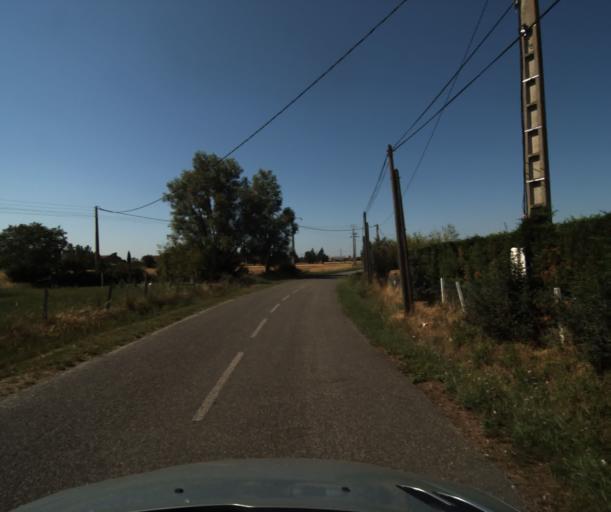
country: FR
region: Midi-Pyrenees
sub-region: Departement de la Haute-Garonne
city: Labarthe-sur-Leze
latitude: 43.4630
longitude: 1.3792
